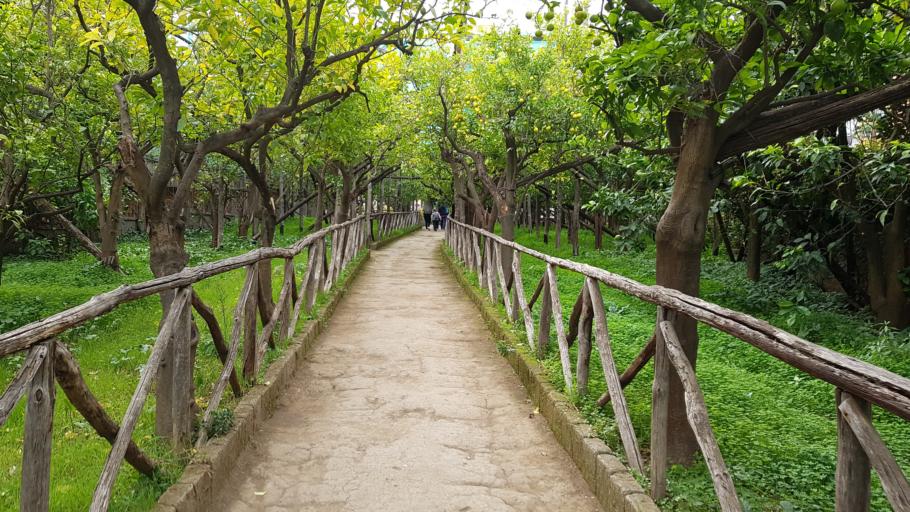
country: IT
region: Campania
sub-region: Provincia di Napoli
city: Sorrento
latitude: 40.6274
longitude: 14.3808
